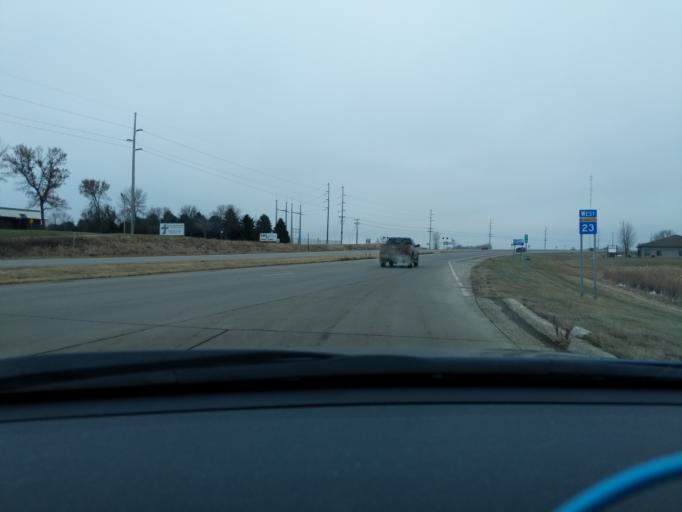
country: US
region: Minnesota
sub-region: Lyon County
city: Marshall
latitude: 44.4500
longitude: -95.7564
